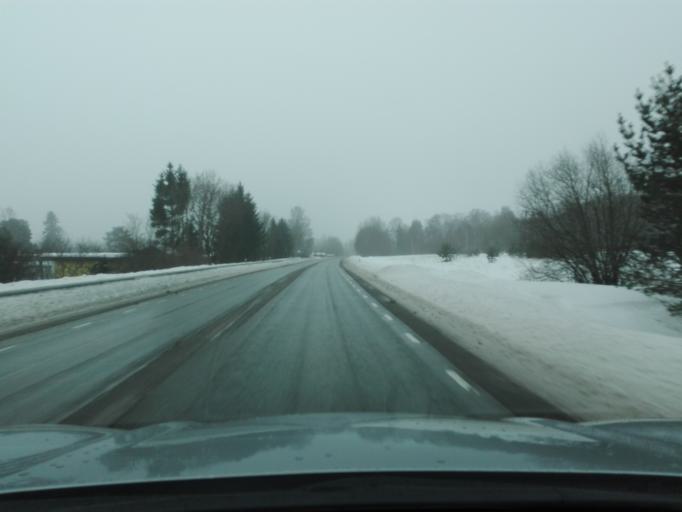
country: EE
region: Harju
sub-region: Kiili vald
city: Kiili
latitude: 59.3311
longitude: 24.7732
